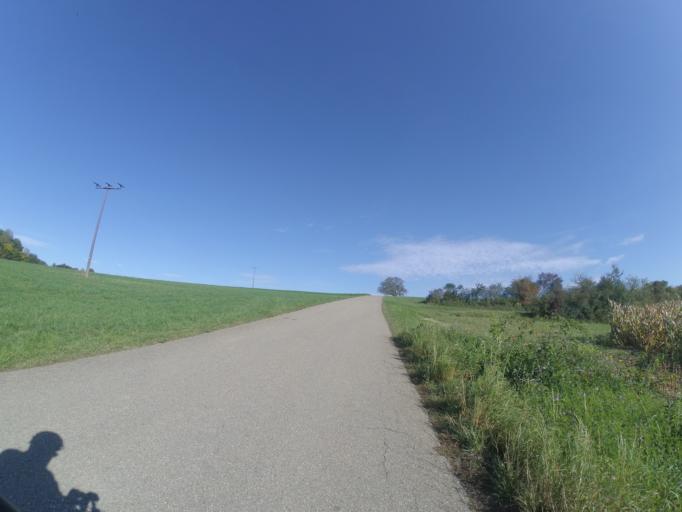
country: DE
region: Baden-Wuerttemberg
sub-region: Tuebingen Region
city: Breitingen
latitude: 48.5219
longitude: 9.9924
